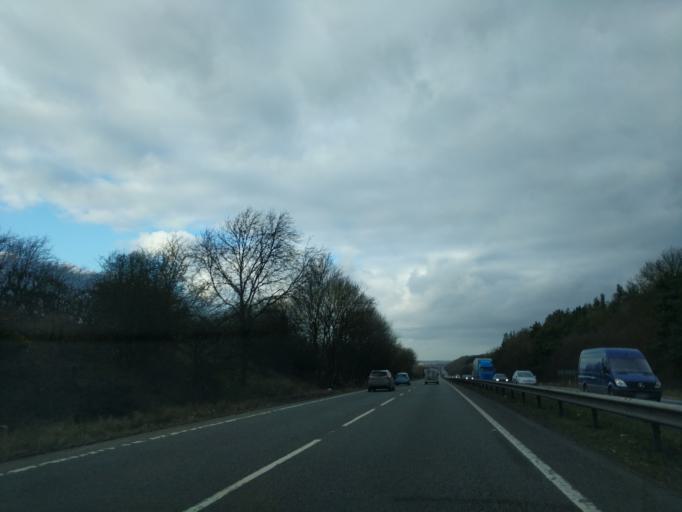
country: GB
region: England
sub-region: Lincolnshire
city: Barrowby
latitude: 52.9236
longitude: -0.6823
